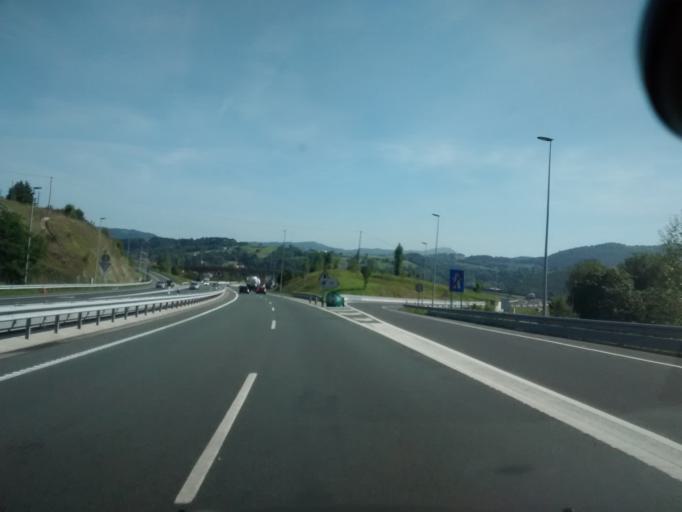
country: ES
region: Basque Country
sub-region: Provincia de Guipuzcoa
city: Astigarraga
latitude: 43.2792
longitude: -1.9622
